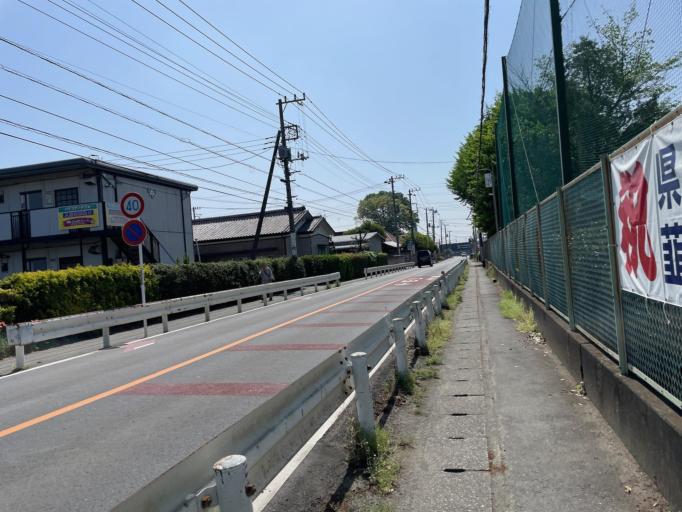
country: JP
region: Gunma
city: Ota
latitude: 36.3040
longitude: 139.4041
